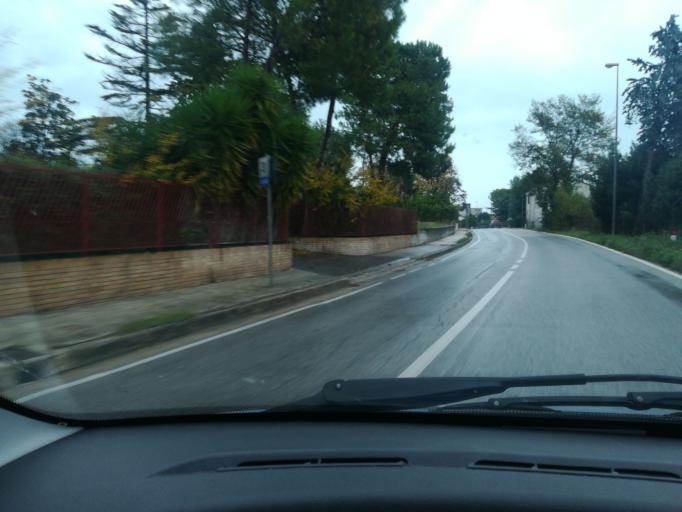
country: IT
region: The Marches
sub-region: Provincia di Macerata
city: Santa Maria Apparente
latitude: 43.2965
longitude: 13.6867
